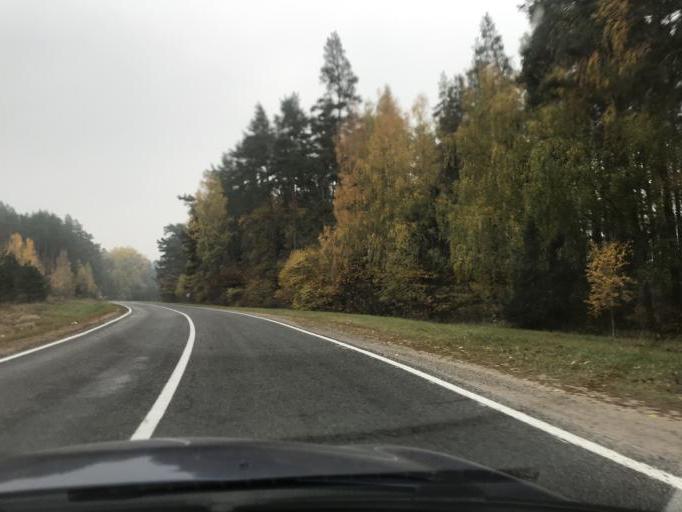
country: BY
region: Grodnenskaya
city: Hrodna
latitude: 53.8454
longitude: 23.8924
